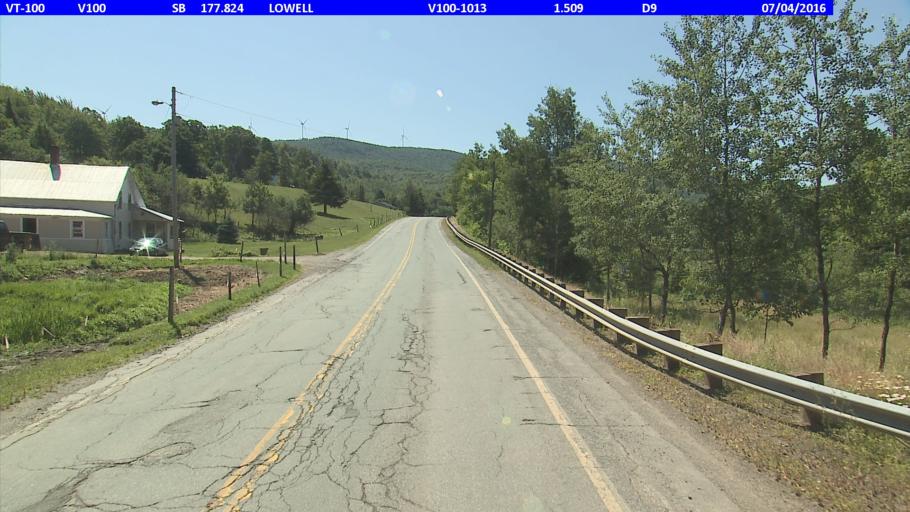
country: US
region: Vermont
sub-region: Lamoille County
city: Hyde Park
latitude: 44.7598
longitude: -72.4572
